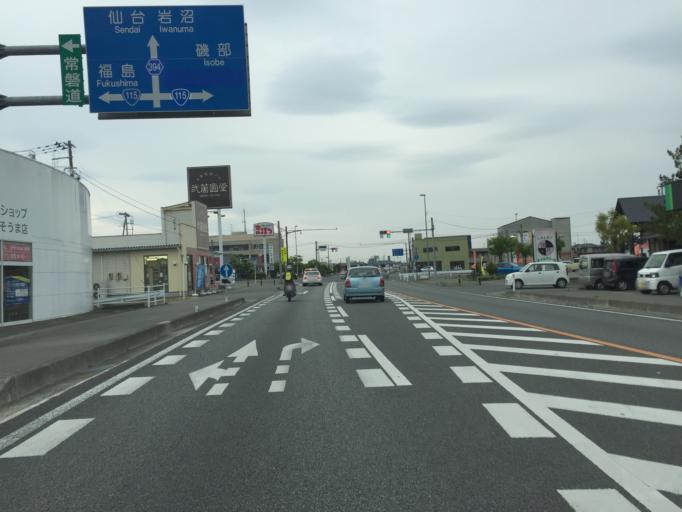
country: JP
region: Miyagi
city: Marumori
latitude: 37.7917
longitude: 140.9294
